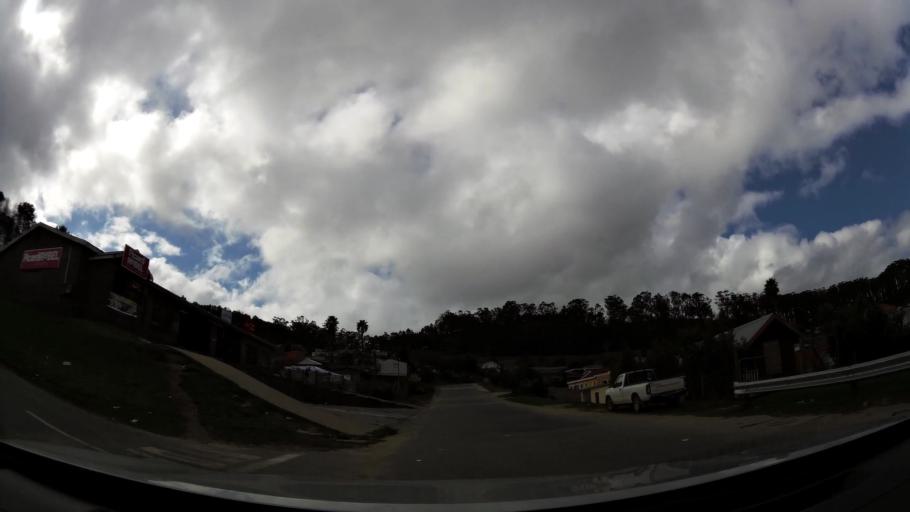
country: ZA
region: Western Cape
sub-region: Eden District Municipality
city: Knysna
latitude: -34.0514
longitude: 23.1036
